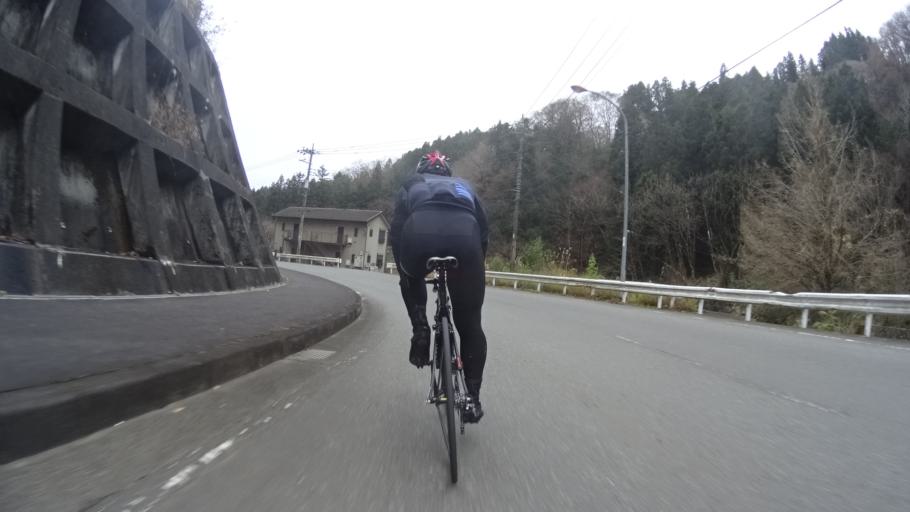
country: JP
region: Yamanashi
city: Uenohara
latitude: 35.6317
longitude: 139.1430
